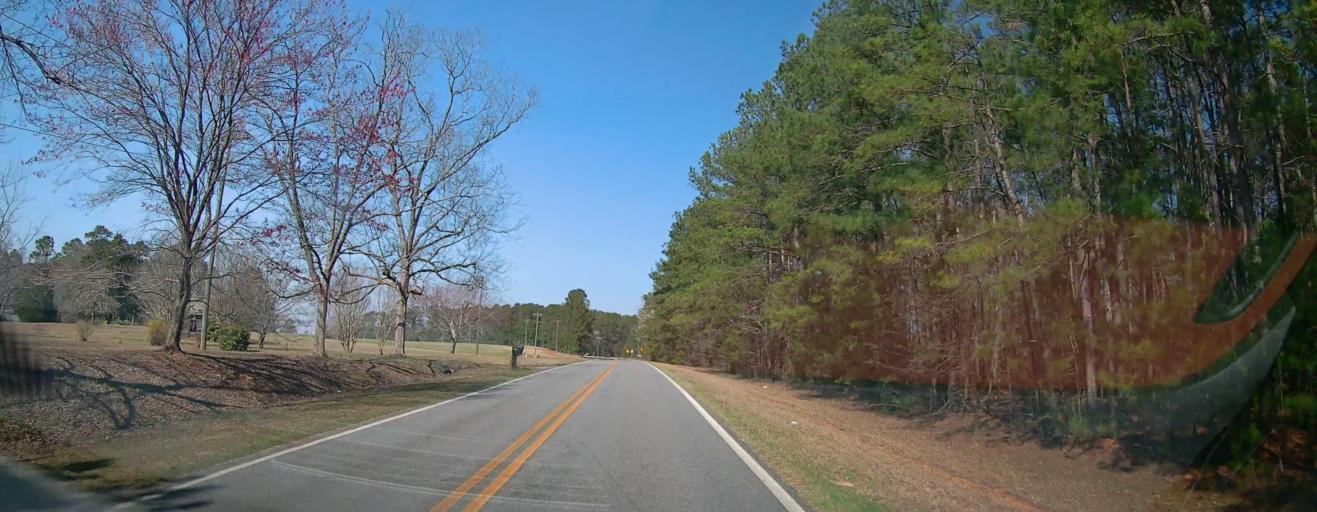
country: US
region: Georgia
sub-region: Jones County
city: Gray
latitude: 32.9756
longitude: -83.5472
